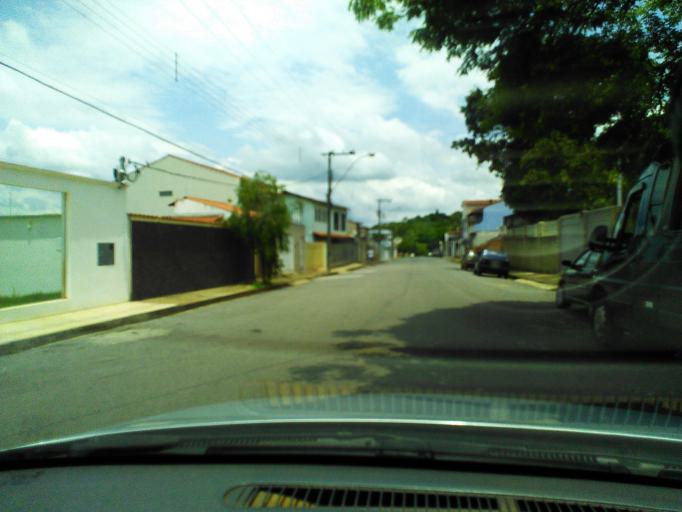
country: BR
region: Minas Gerais
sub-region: Tres Coracoes
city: Tres Coracoes
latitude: -21.6946
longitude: -45.2620
